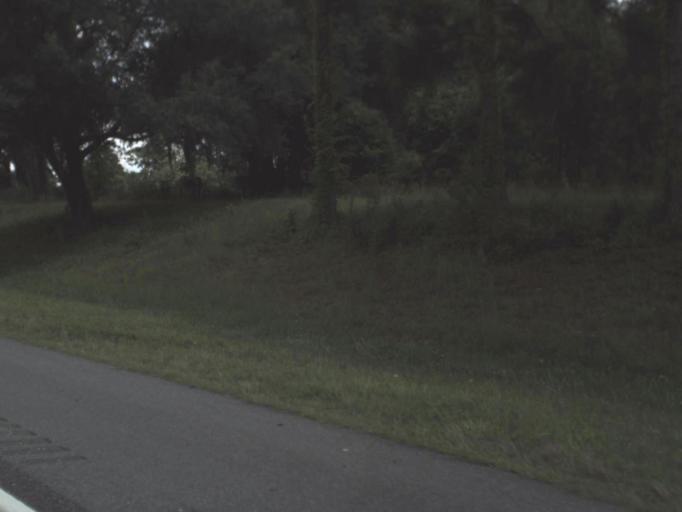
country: US
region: Florida
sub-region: Hamilton County
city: Jasper
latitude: 30.4862
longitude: -83.0064
